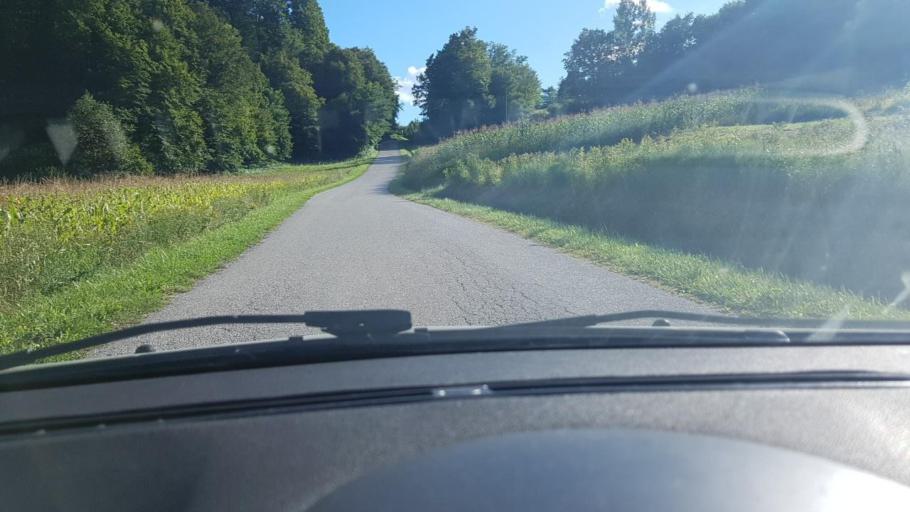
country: HR
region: Krapinsko-Zagorska
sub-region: Grad Krapina
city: Krapina
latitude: 46.1510
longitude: 15.8420
